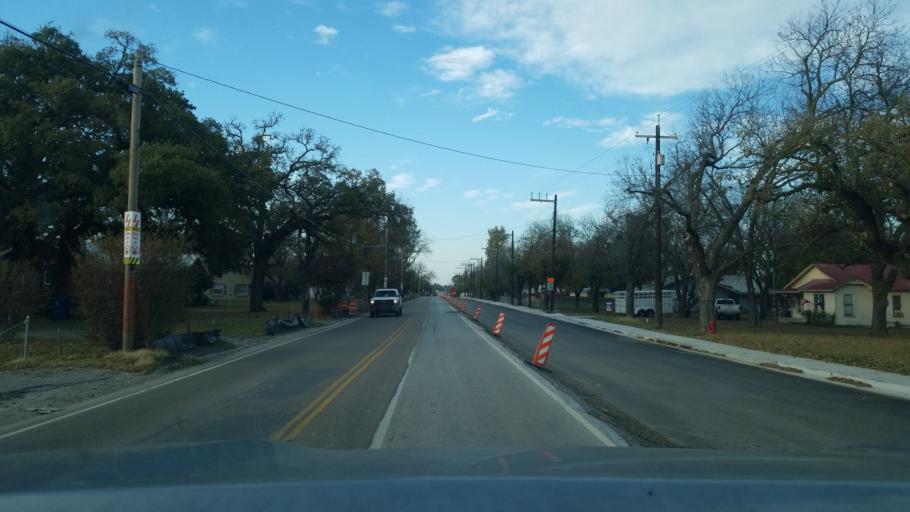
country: US
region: Texas
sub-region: Brown County
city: Lake Brownwood
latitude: 32.0878
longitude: -98.9641
